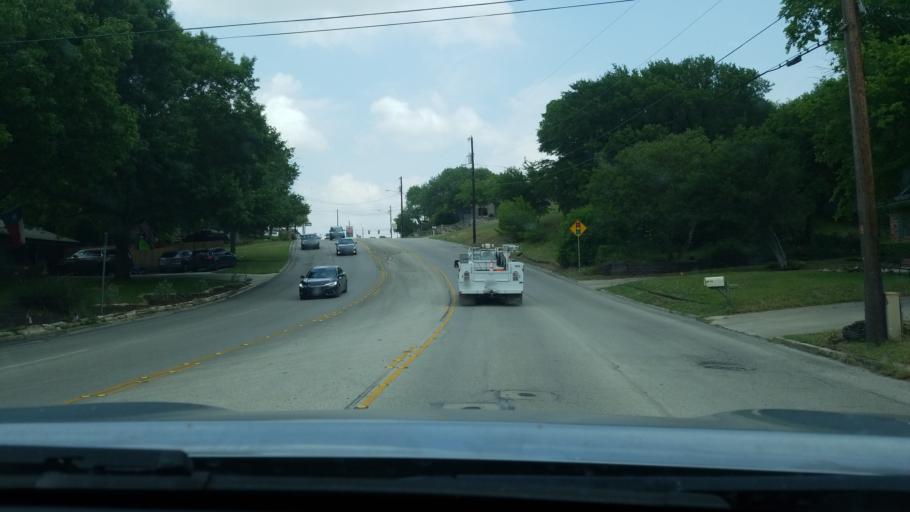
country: US
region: Texas
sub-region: Comal County
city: New Braunfels
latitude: 29.7183
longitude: -98.1061
